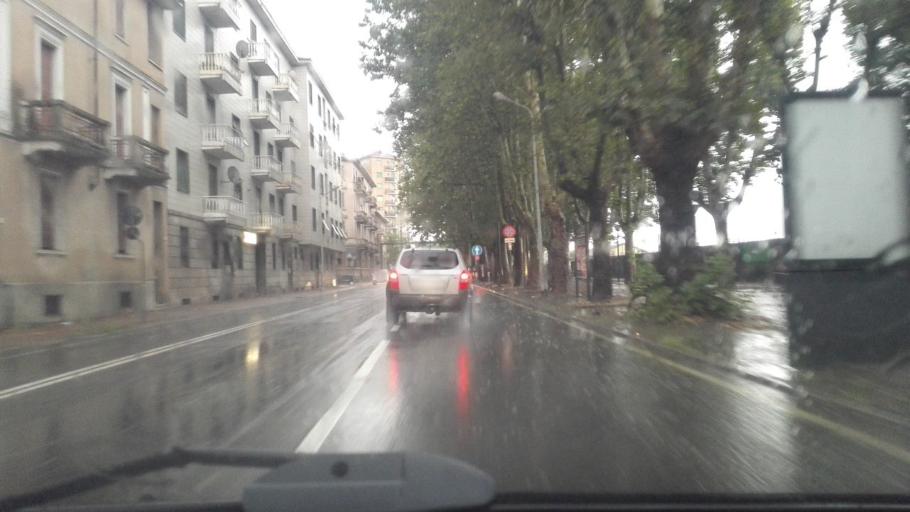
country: IT
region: Piedmont
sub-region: Provincia di Alessandria
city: Alessandria
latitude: 44.9132
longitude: 8.6035
